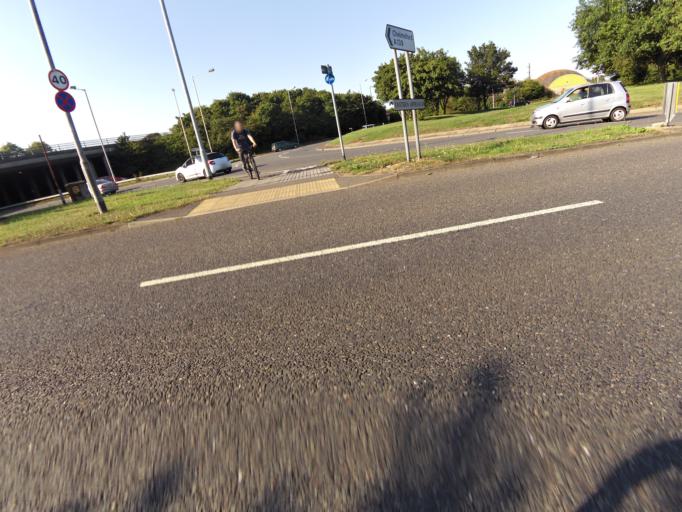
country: GB
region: England
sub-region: Essex
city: Chelmsford
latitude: 51.7469
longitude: 0.5046
